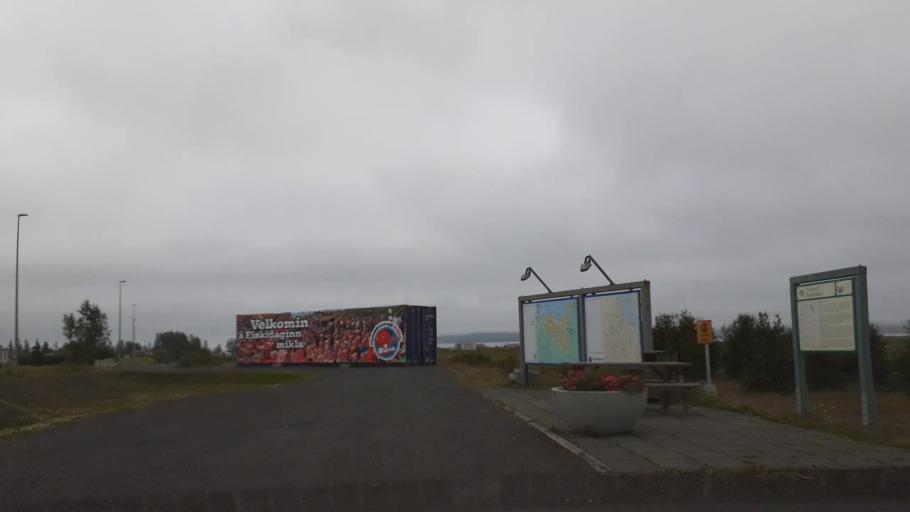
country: IS
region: Northeast
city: Dalvik
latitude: 65.9635
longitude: -18.5344
